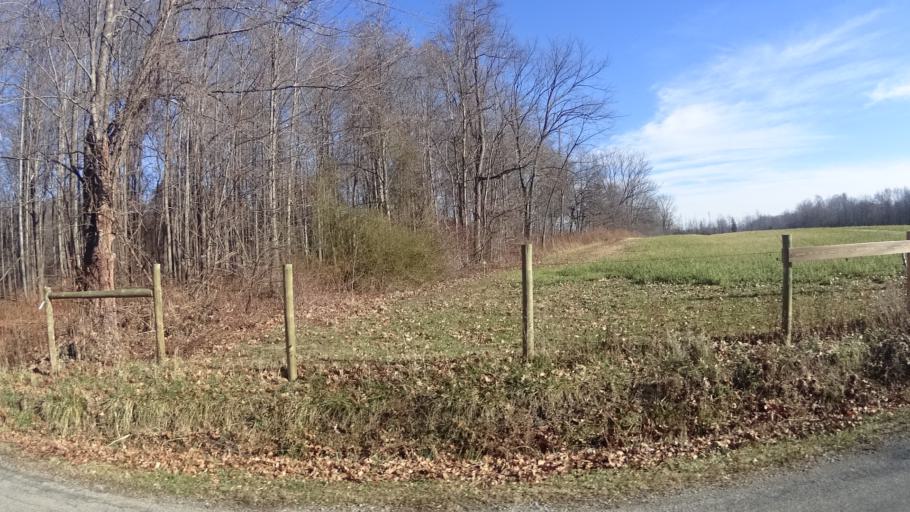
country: US
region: Ohio
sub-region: Lorain County
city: South Amherst
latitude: 41.3511
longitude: -82.2909
